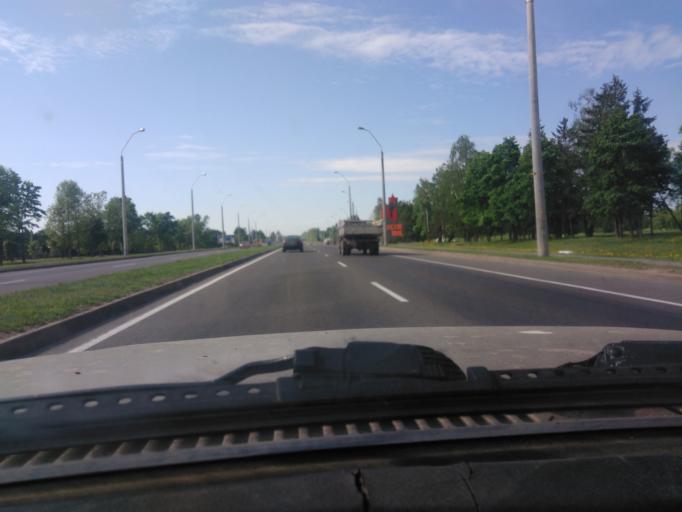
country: BY
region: Mogilev
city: Buynichy
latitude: 53.8651
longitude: 30.2596
